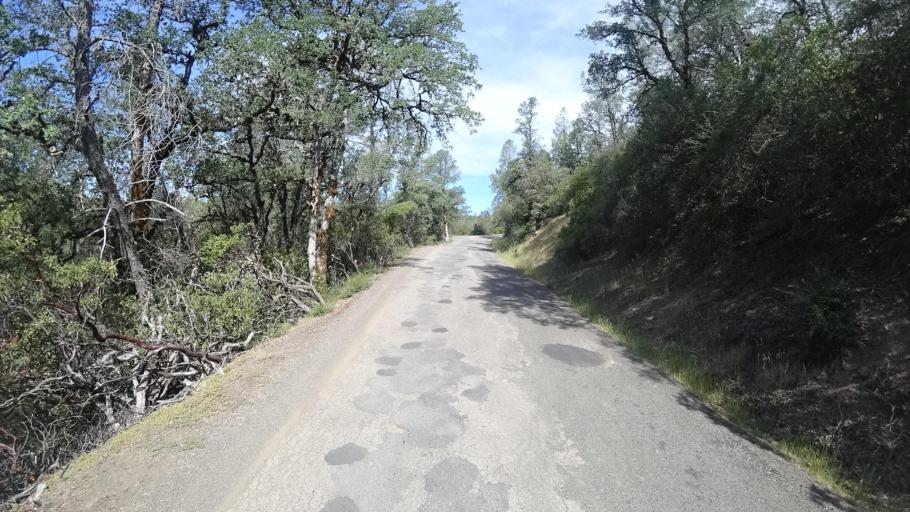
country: US
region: California
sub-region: Lake County
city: Cobb
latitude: 38.8634
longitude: -122.7427
